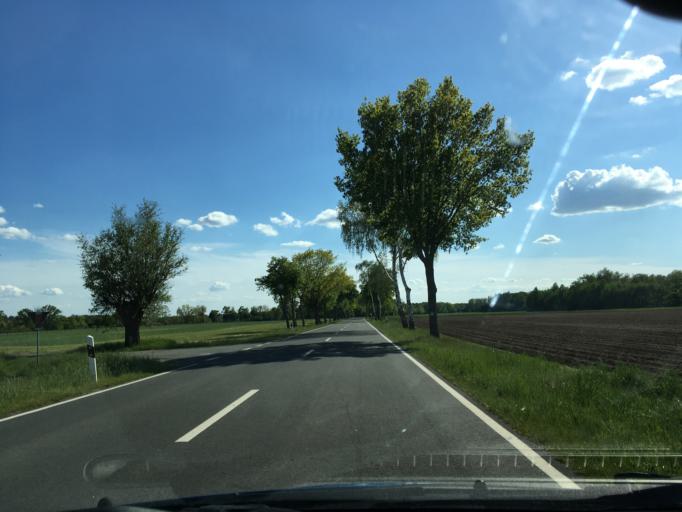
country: DE
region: Brandenburg
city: Lanz
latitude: 53.0243
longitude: 11.5583
